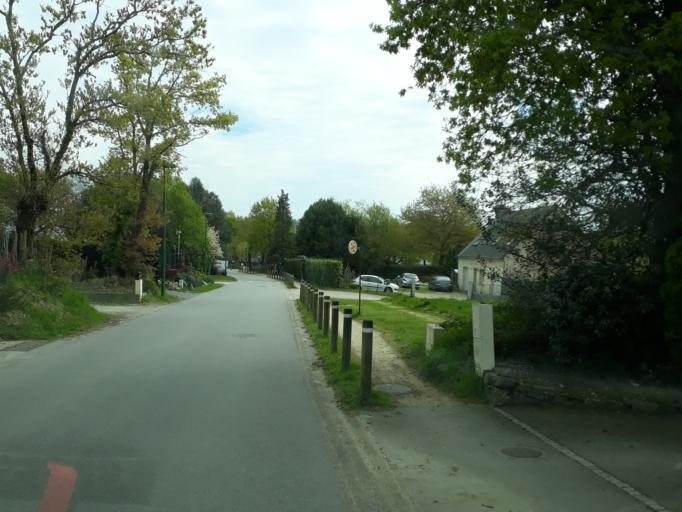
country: FR
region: Brittany
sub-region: Departement du Morbihan
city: Surzur
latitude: 47.5818
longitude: -2.6403
